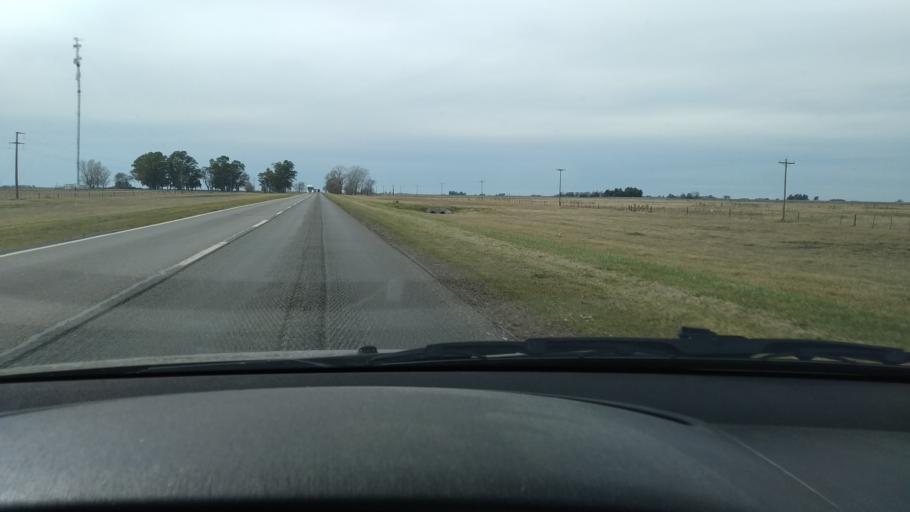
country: AR
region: Buenos Aires
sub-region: Partido de Azul
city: Azul
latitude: -36.7347
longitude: -59.7842
